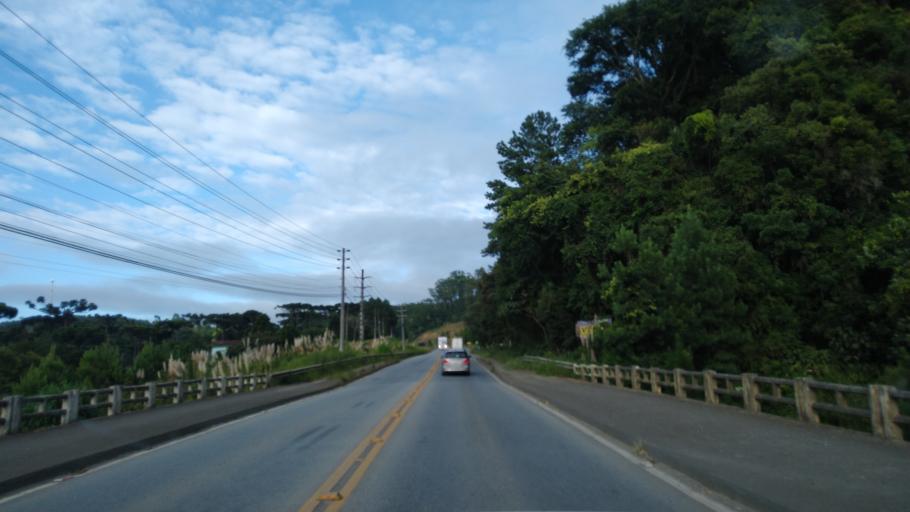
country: BR
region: Santa Catarina
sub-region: Sao Bento Do Sul
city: Sao Bento do Sul
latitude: -26.2281
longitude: -49.4207
